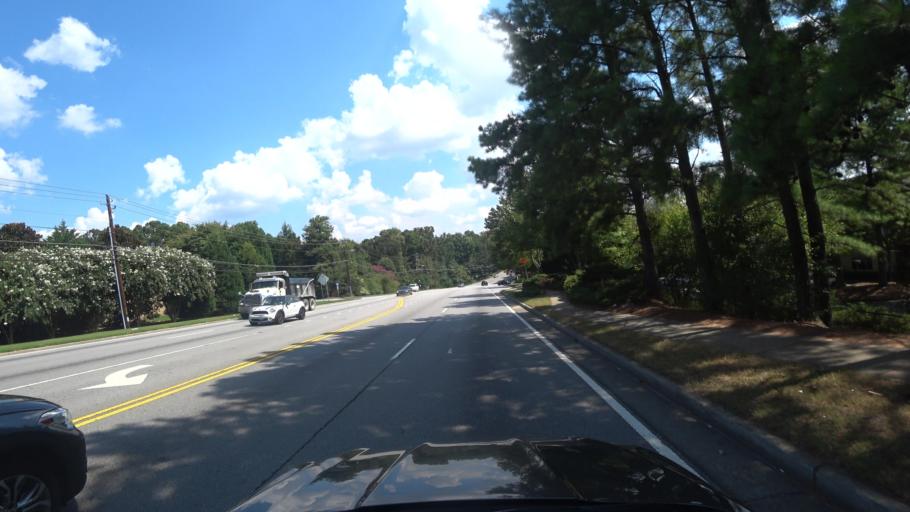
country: US
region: Georgia
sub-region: Gwinnett County
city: Norcross
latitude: 33.9585
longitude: -84.2463
